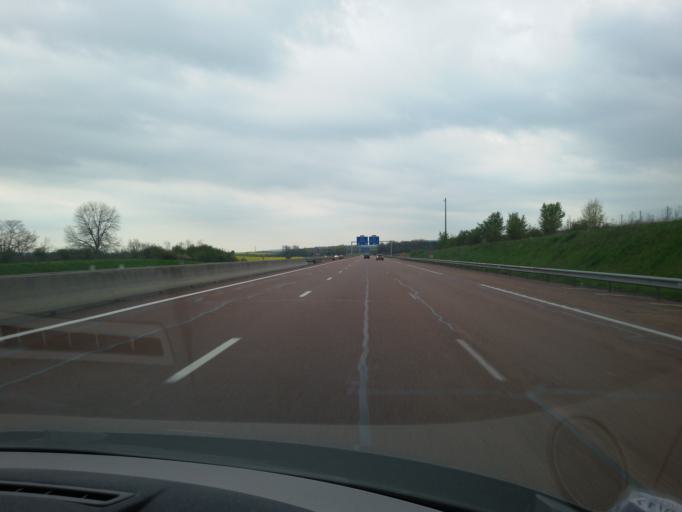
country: FR
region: Champagne-Ardenne
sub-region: Departement de la Haute-Marne
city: Rolampont
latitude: 47.9013
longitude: 5.2237
